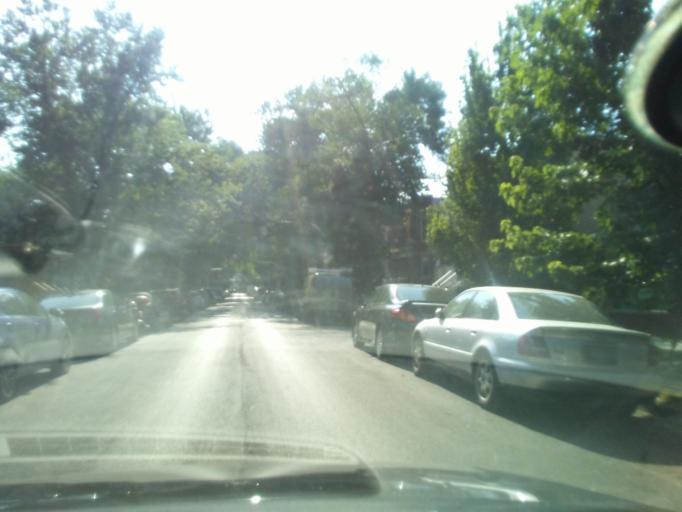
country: US
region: Illinois
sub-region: Cook County
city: Lincolnwood
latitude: 41.9743
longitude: -87.6713
